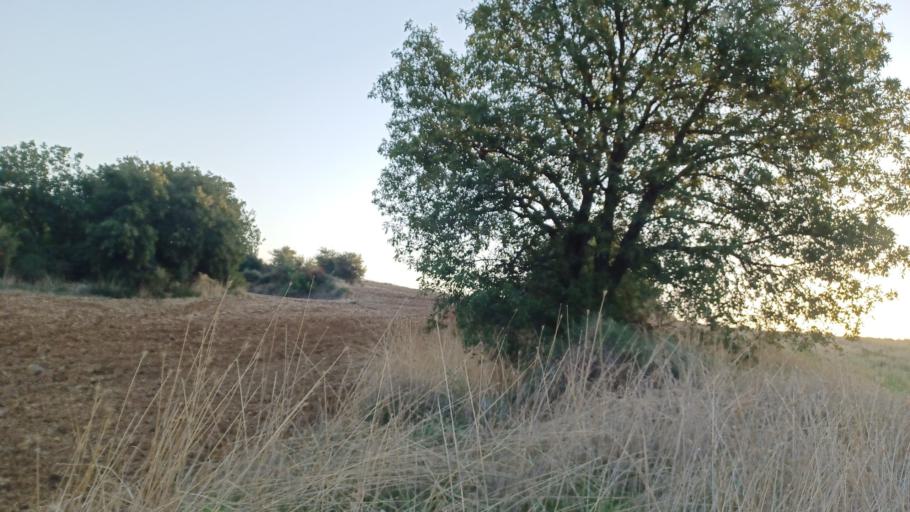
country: CY
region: Pafos
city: Polis
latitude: 35.0010
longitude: 32.4493
